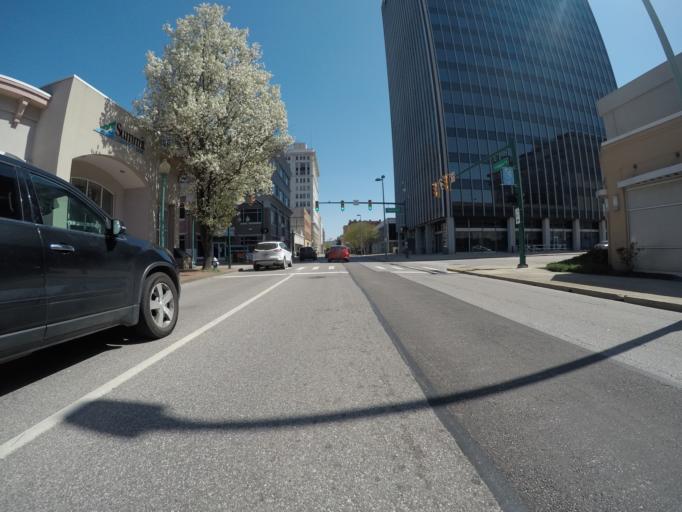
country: US
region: West Virginia
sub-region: Kanawha County
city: Charleston
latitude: 38.3501
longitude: -81.6370
